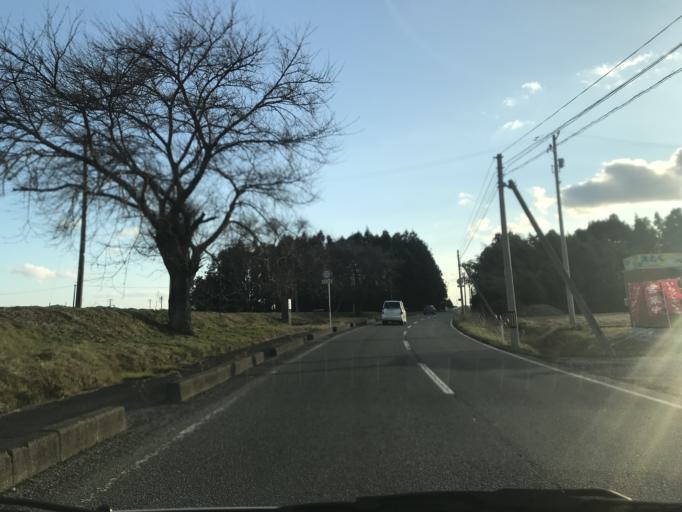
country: JP
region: Miyagi
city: Kogota
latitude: 38.6490
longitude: 141.0758
